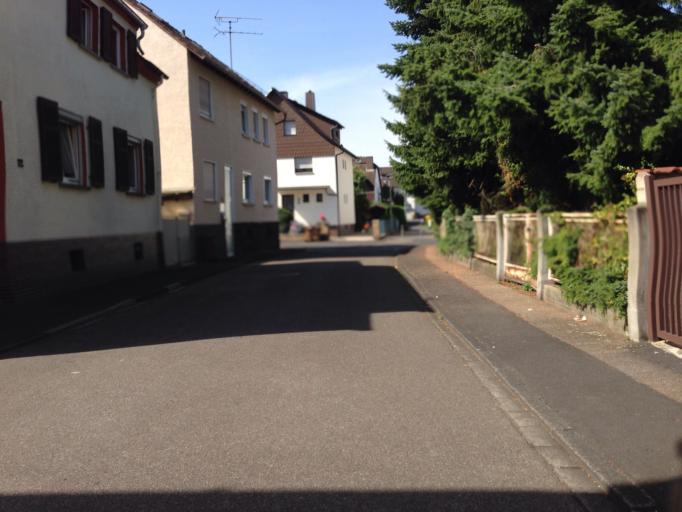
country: DE
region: Hesse
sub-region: Regierungsbezirk Darmstadt
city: Hanau am Main
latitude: 50.1153
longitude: 8.9080
